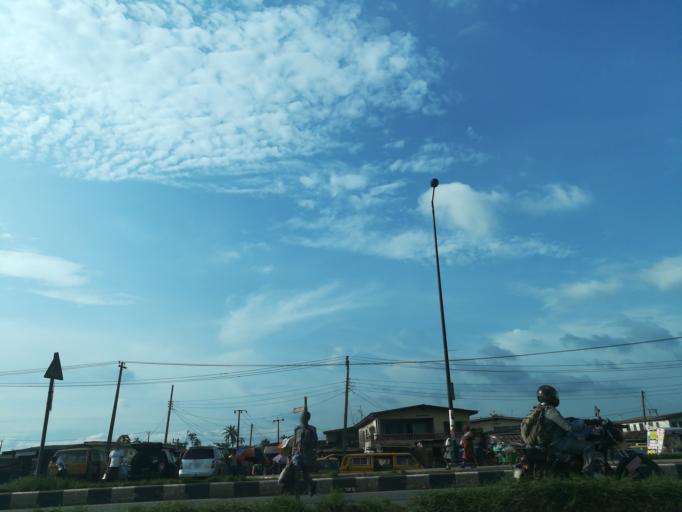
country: NG
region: Lagos
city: Ojota
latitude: 6.6092
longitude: 3.4282
